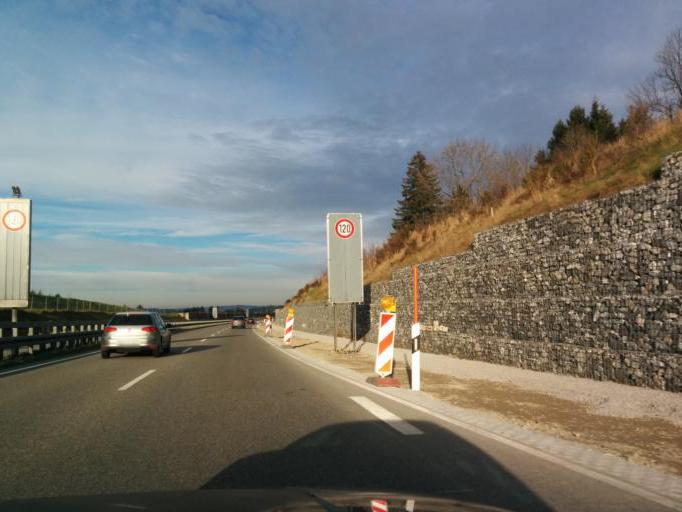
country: DE
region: Bavaria
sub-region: Swabia
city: Waltenhofen
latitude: 47.6323
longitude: 10.2815
